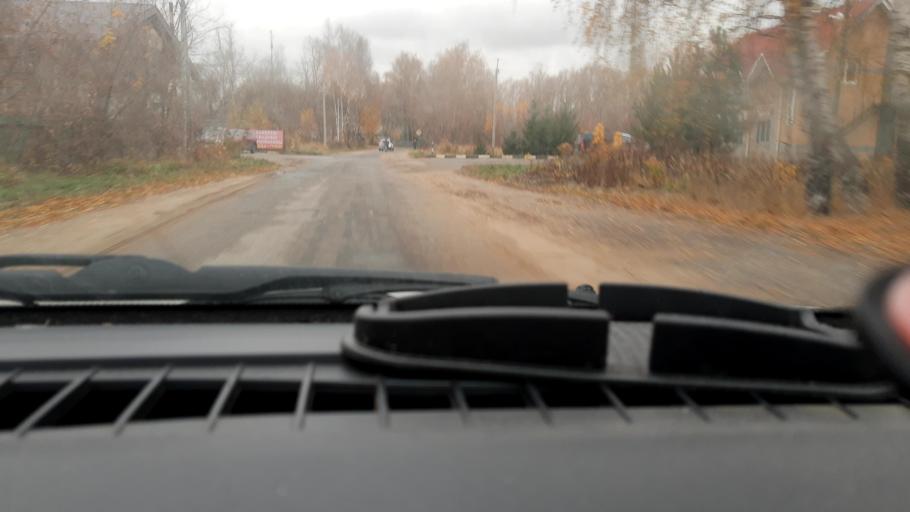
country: RU
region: Nizjnij Novgorod
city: Sitniki
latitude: 56.4110
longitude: 44.0332
